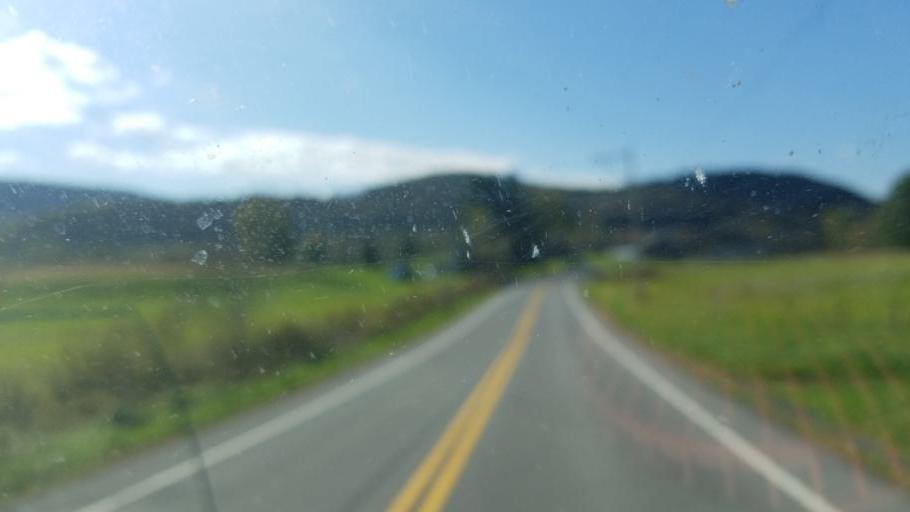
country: US
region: Pennsylvania
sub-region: Blair County
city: Claysburg
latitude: 40.1887
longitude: -78.4980
